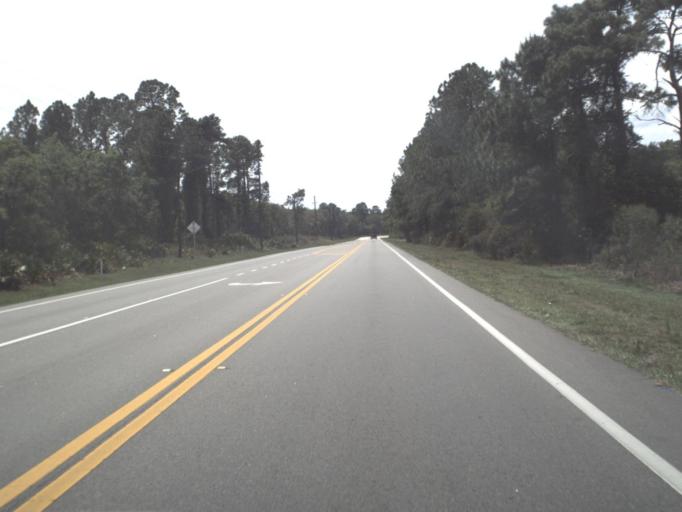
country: US
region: Florida
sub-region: Lake County
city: Lake Mack-Forest Hills
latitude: 28.9186
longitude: -81.4449
